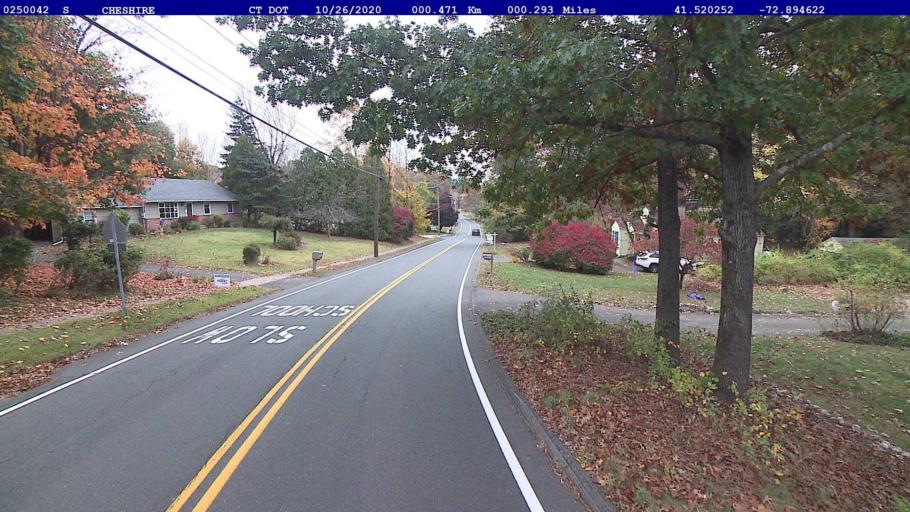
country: US
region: Connecticut
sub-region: New Haven County
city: Cheshire Village
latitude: 41.5202
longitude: -72.8946
